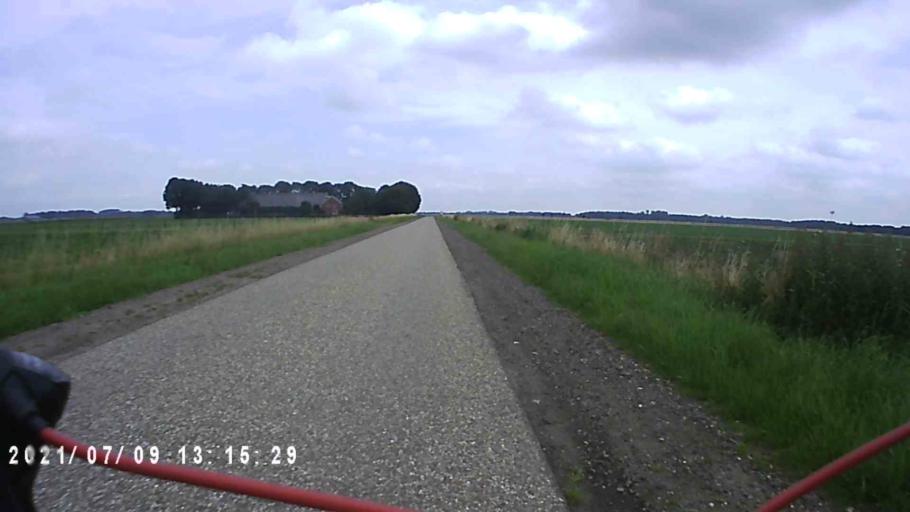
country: NL
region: Groningen
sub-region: Gemeente Vlagtwedde
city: Vlagtwedde
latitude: 53.1192
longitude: 7.1422
